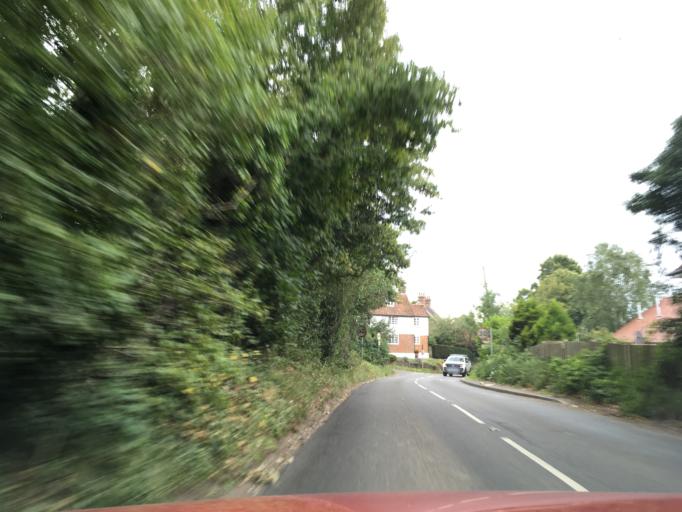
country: GB
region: England
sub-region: Kent
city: Yalding
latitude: 51.2292
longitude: 0.4340
